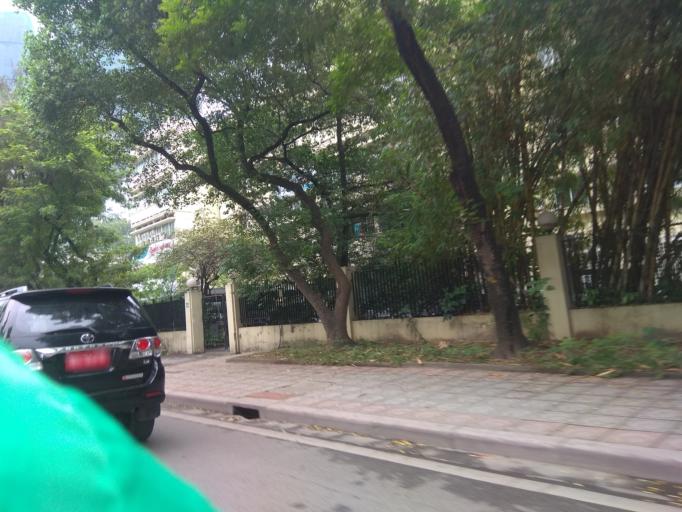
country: VN
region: Ha Noi
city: Dong Da
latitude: 21.0311
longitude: 105.8186
